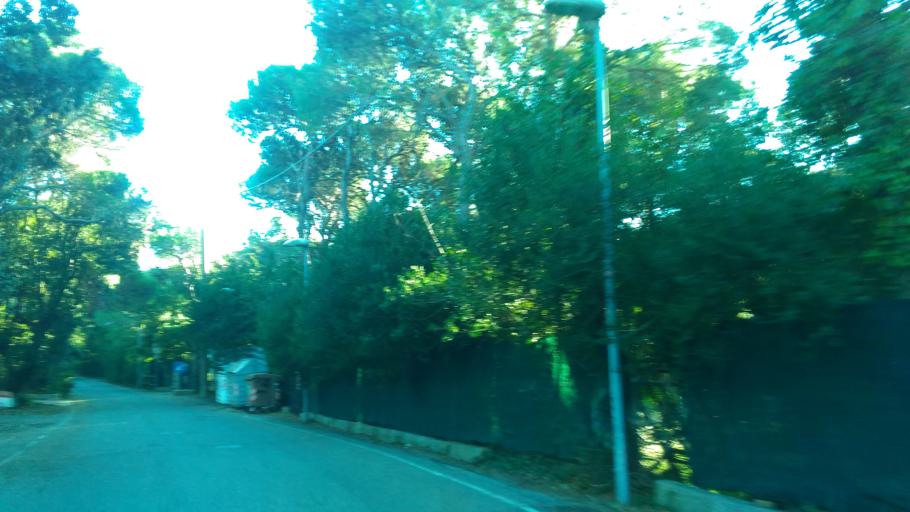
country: IT
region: Tuscany
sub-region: Provincia di Livorno
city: Quercianella
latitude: 43.4607
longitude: 10.3622
